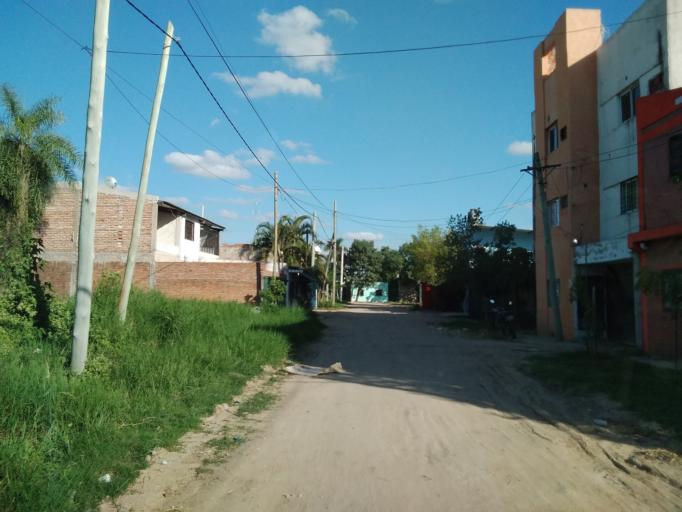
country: AR
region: Corrientes
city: Corrientes
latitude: -27.4624
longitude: -58.7793
